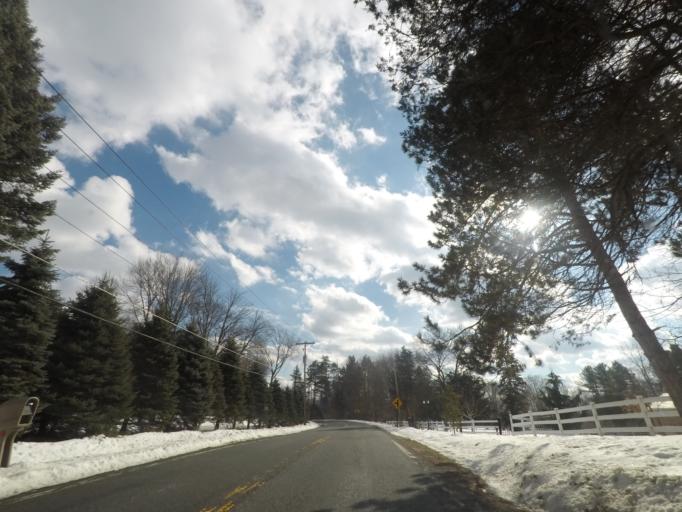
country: US
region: New York
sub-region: Schenectady County
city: Niskayuna
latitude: 42.8372
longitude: -73.8727
